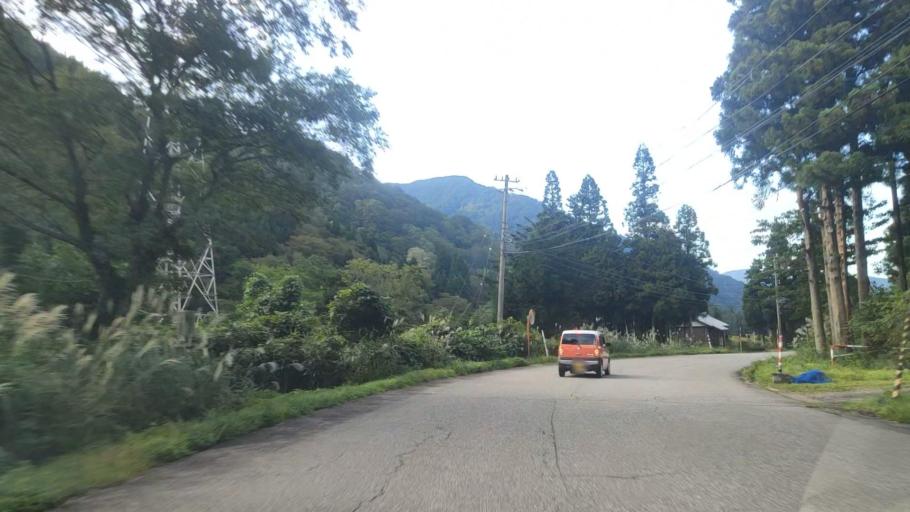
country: JP
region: Toyama
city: Yatsuomachi-higashikumisaka
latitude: 36.4470
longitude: 137.0835
